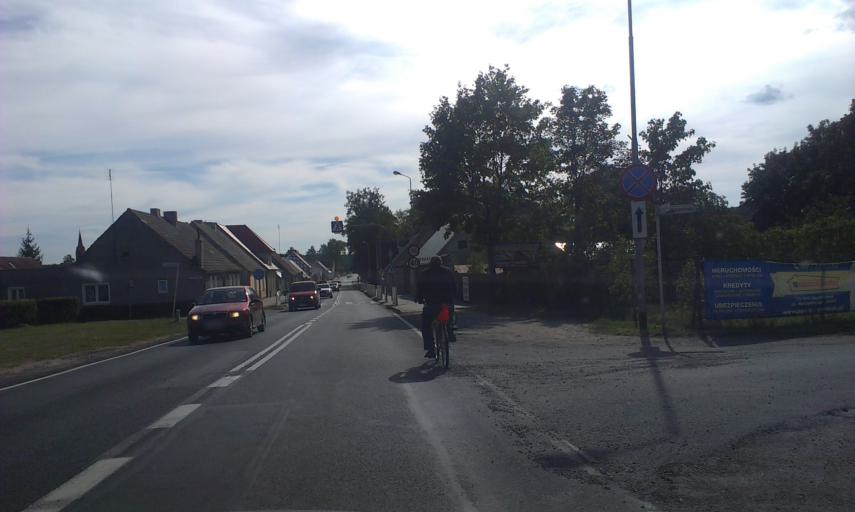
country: PL
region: Greater Poland Voivodeship
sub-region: Powiat zlotowski
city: Okonek
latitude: 53.5392
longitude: 16.8487
